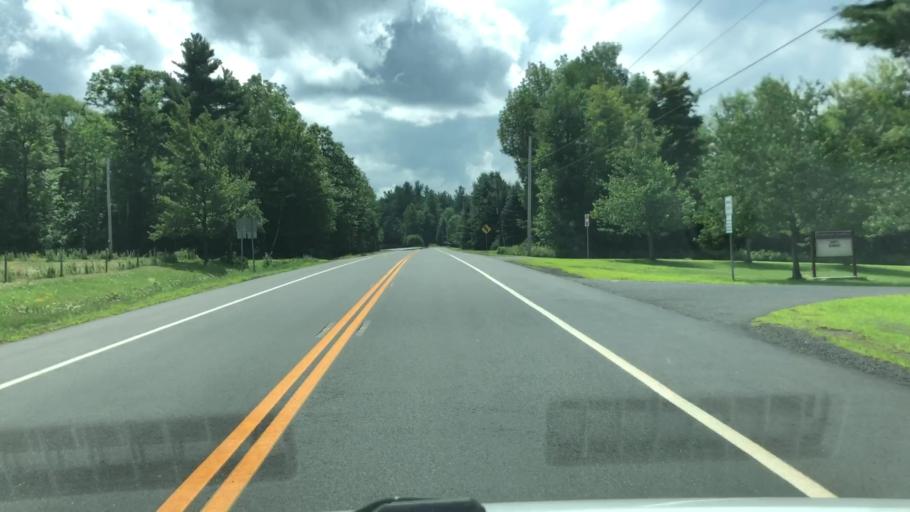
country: US
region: Massachusetts
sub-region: Franklin County
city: Ashfield
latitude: 42.5079
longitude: -72.8100
